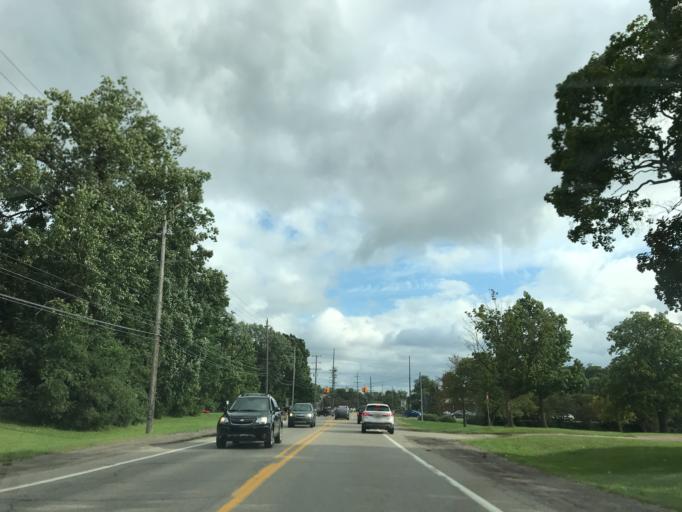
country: US
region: Michigan
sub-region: Wayne County
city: Northville
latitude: 42.4127
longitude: -83.4697
